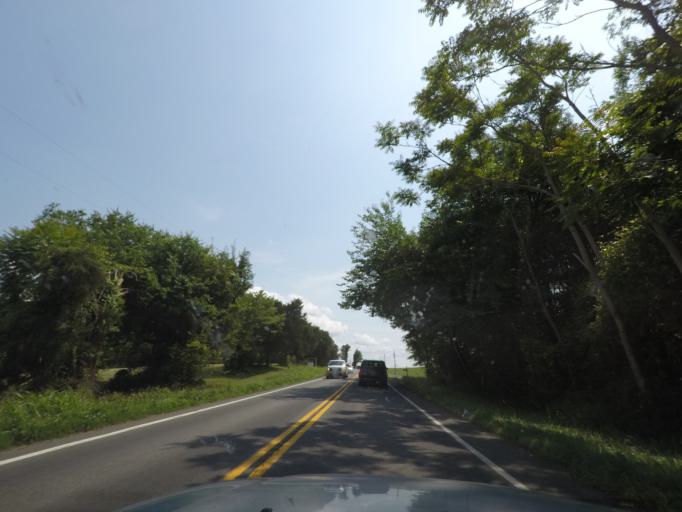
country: US
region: Virginia
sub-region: Orange County
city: Orange
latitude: 38.3092
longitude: -78.1313
